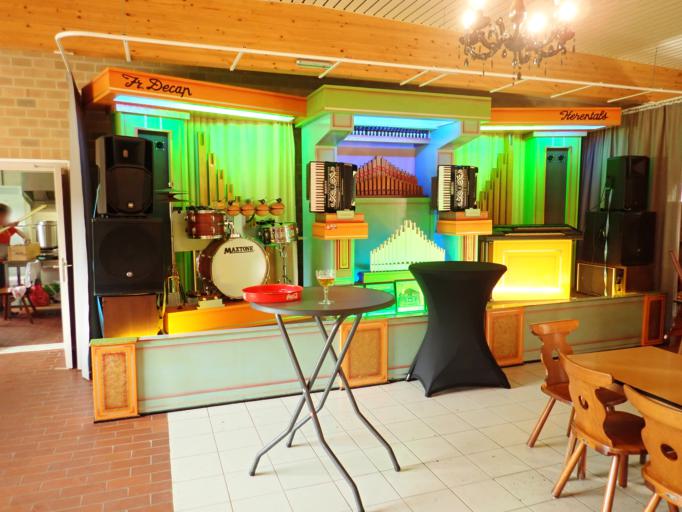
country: BE
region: Flanders
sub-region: Provincie Antwerpen
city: Vorselaar
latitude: 51.1905
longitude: 4.7924
